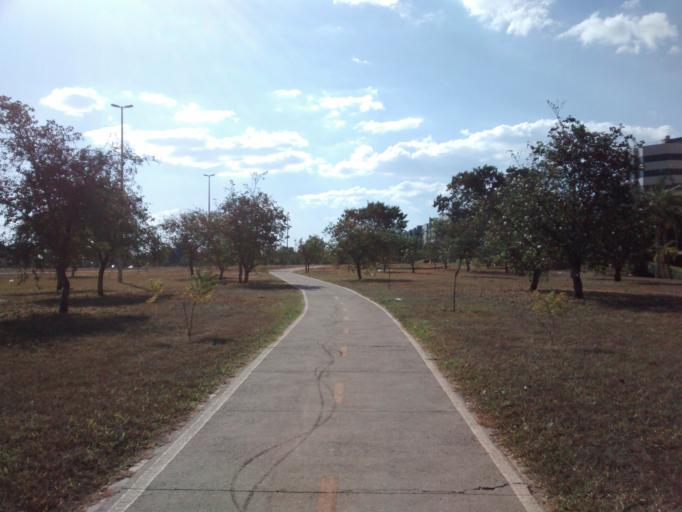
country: BR
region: Federal District
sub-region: Brasilia
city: Brasilia
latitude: -15.8020
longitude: -47.9309
